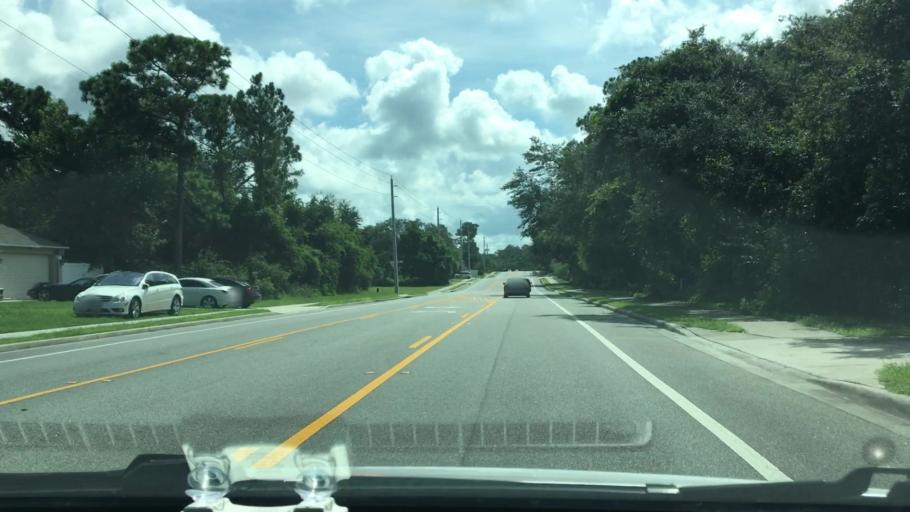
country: US
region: Florida
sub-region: Volusia County
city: Deltona
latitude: 28.8780
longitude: -81.1827
